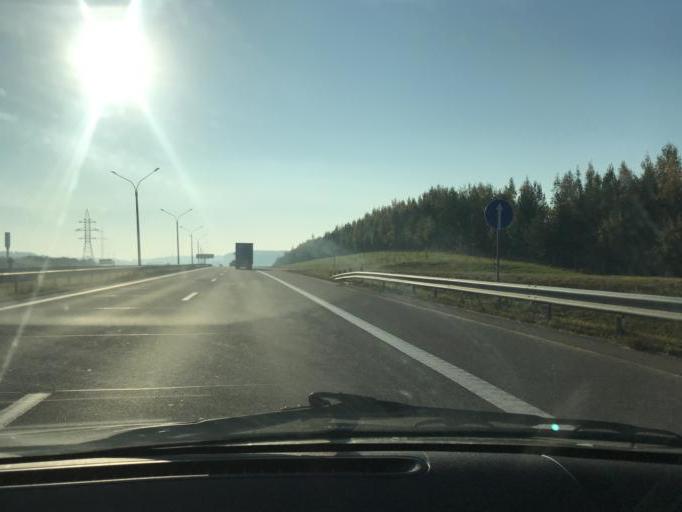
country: BY
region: Minsk
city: Slabada
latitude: 53.9912
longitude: 27.9202
